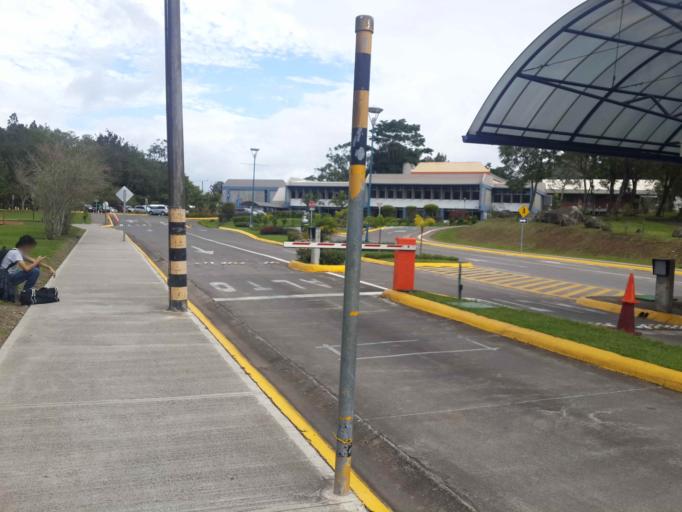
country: CR
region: Cartago
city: Cartago
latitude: 9.8579
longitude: -83.9129
